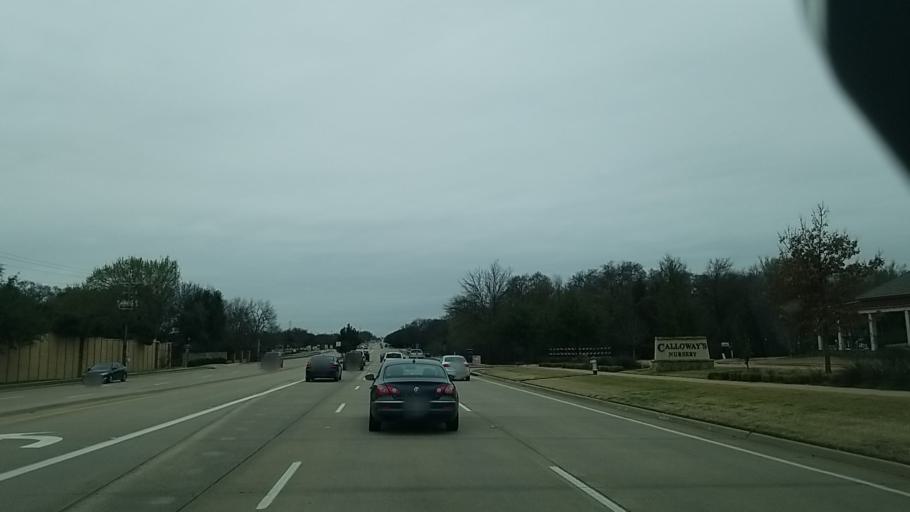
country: US
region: Texas
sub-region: Denton County
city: Flower Mound
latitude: 33.0245
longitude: -97.0709
